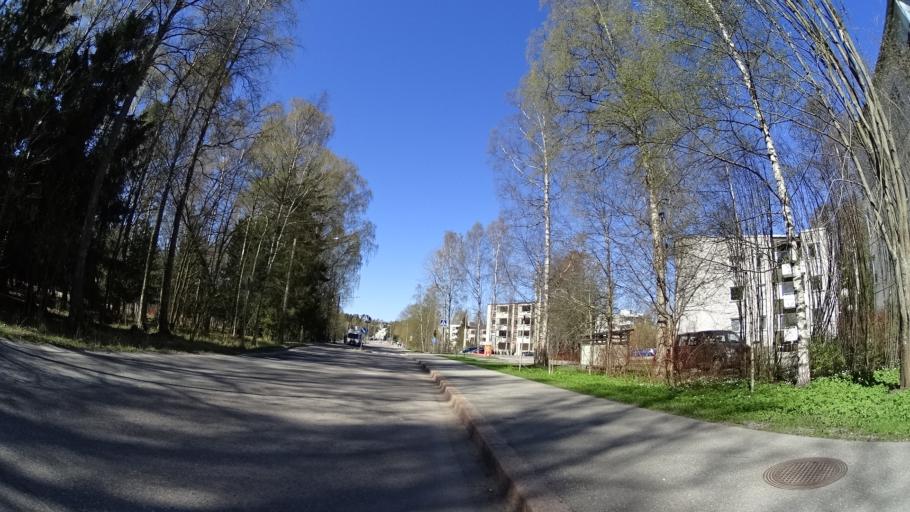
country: FI
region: Uusimaa
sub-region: Helsinki
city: Koukkuniemi
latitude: 60.1625
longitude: 24.7830
